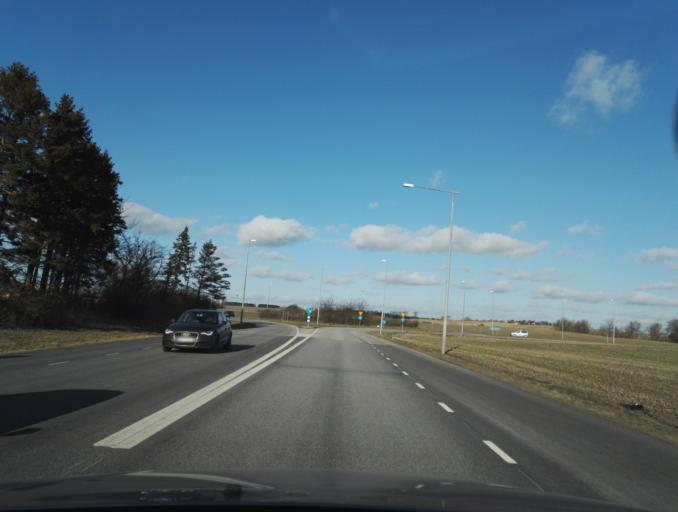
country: SE
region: Skane
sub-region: Svedala Kommun
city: Svedala
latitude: 55.4518
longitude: 13.1874
